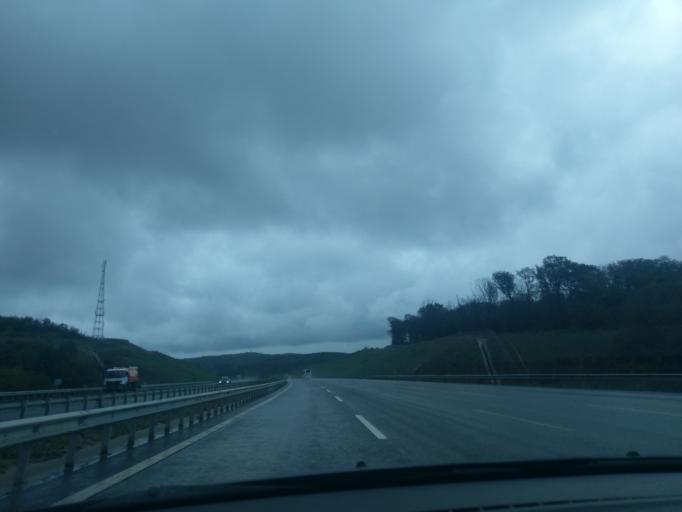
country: TR
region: Istanbul
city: Kemerburgaz
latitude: 41.2311
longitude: 28.9303
